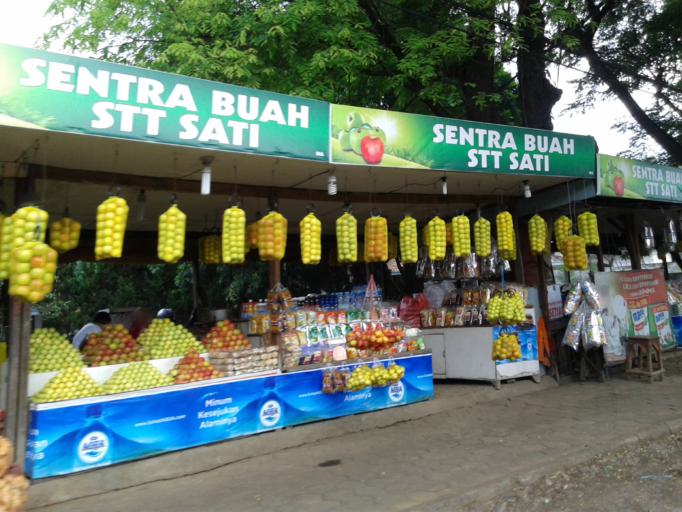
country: ID
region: East Java
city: Singosari
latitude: -7.9250
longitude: 112.6517
